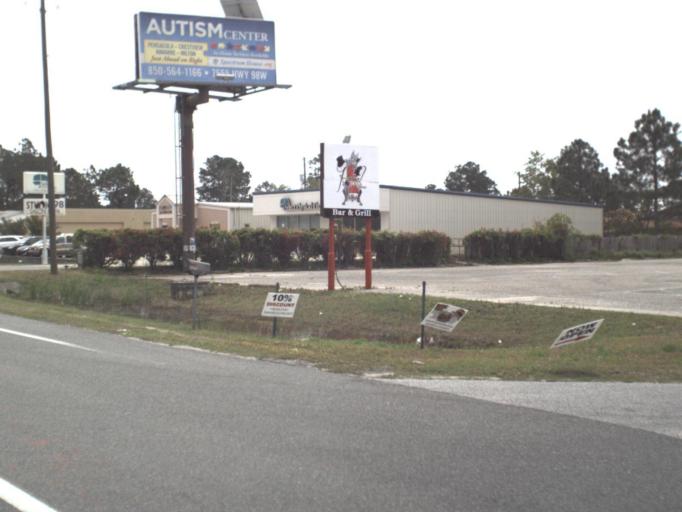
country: US
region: Florida
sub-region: Escambia County
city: Myrtle Grove
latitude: 30.3996
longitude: -87.3121
